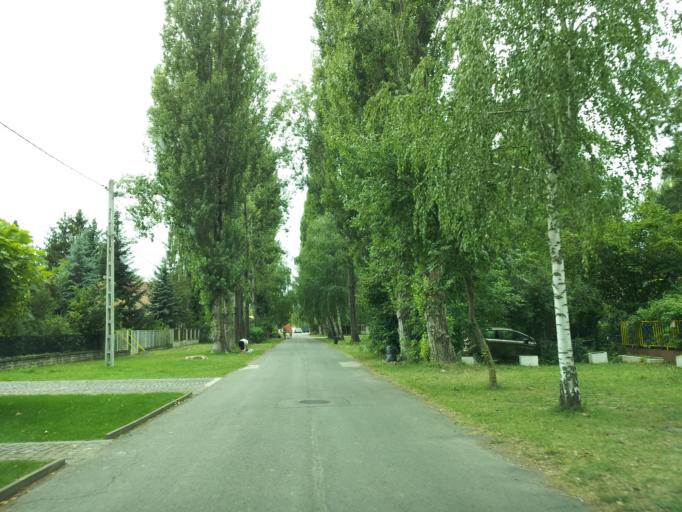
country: HU
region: Somogy
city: Zamardi
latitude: 46.8821
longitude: 17.9319
